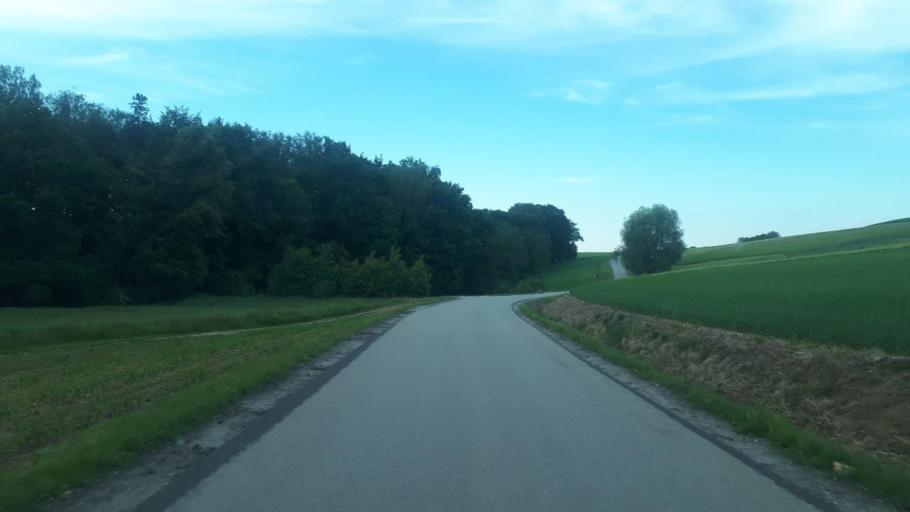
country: PL
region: Silesian Voivodeship
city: Janowice
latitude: 49.8989
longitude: 19.1093
